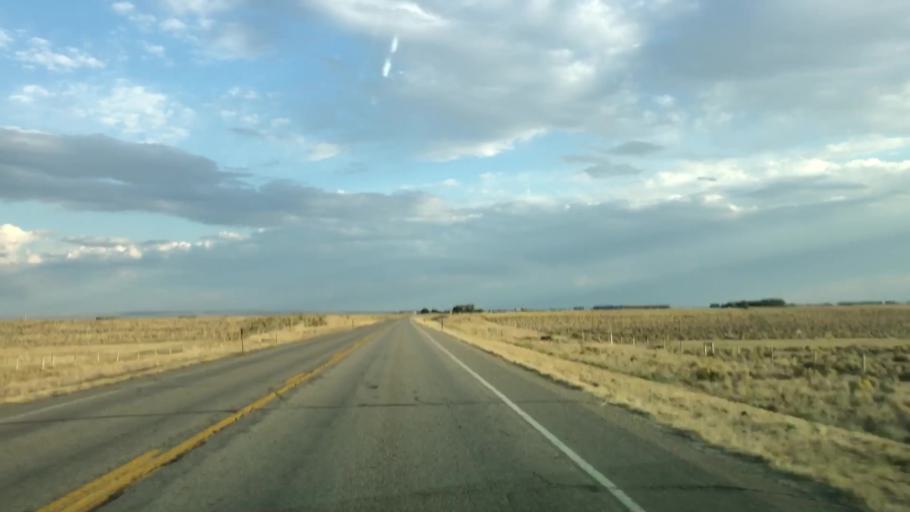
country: US
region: Wyoming
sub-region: Sweetwater County
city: North Rock Springs
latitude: 42.0936
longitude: -109.4426
